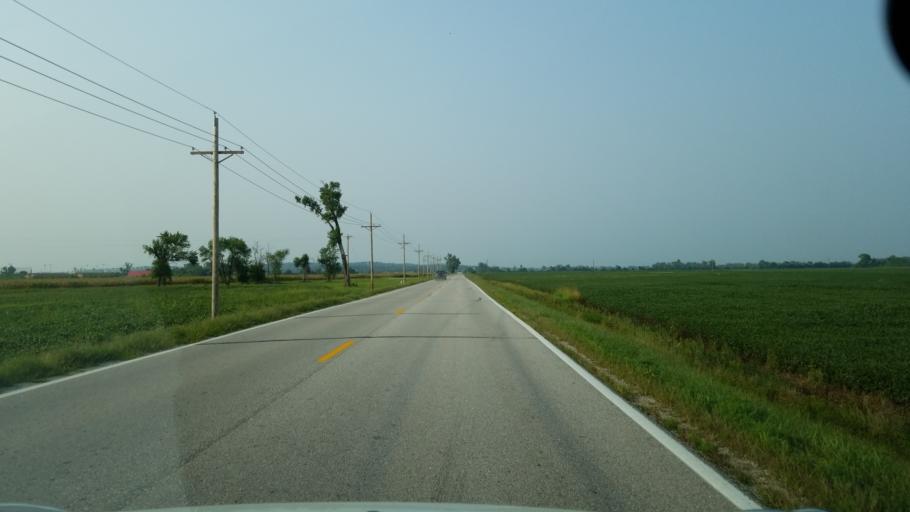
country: US
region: Nebraska
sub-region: Sarpy County
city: Offutt Air Force Base
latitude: 41.0960
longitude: -95.8898
